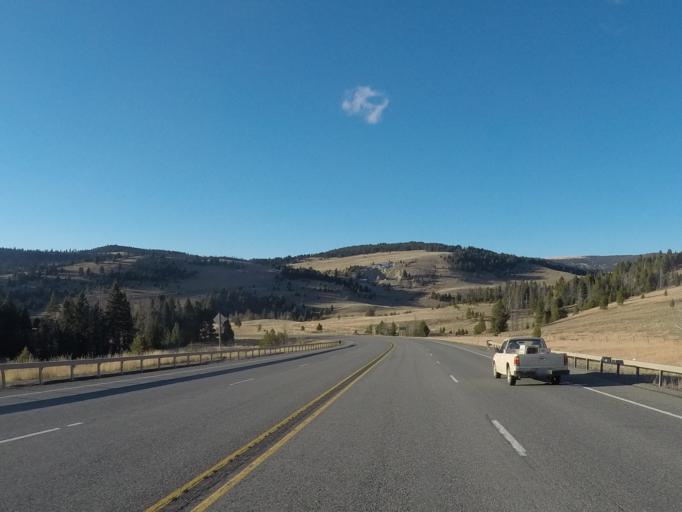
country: US
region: Montana
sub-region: Lewis and Clark County
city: Helena West Side
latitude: 46.5596
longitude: -112.3717
